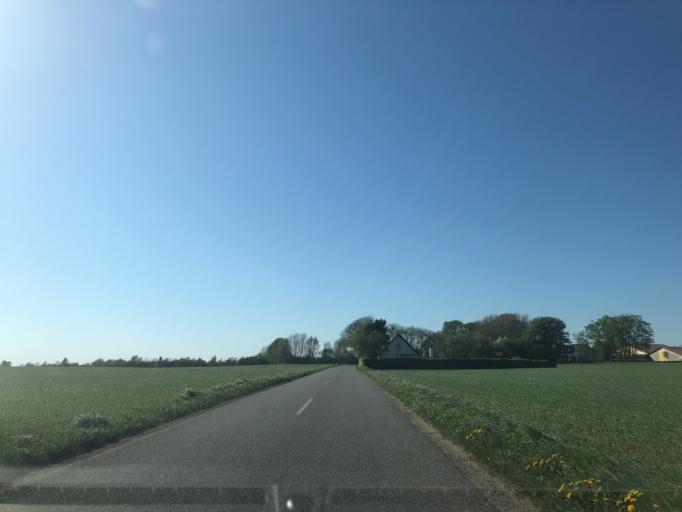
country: DK
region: Zealand
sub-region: Ringsted Kommune
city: Ringsted
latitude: 55.4676
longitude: 11.6979
